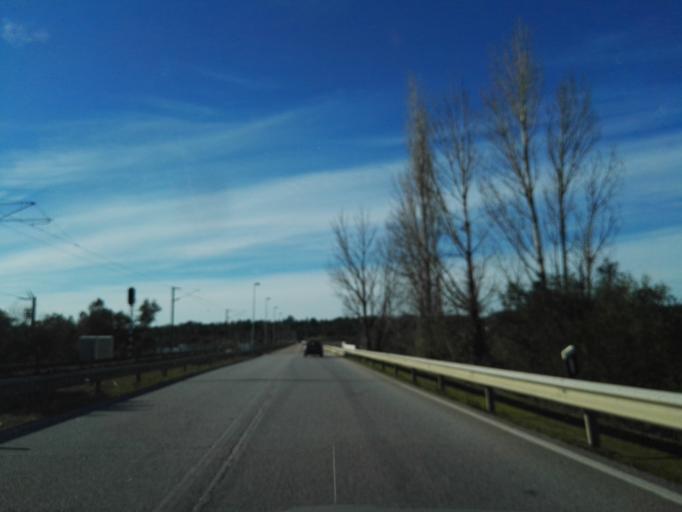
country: PT
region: Santarem
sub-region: Abrantes
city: Alferrarede
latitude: 39.4696
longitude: -8.0621
